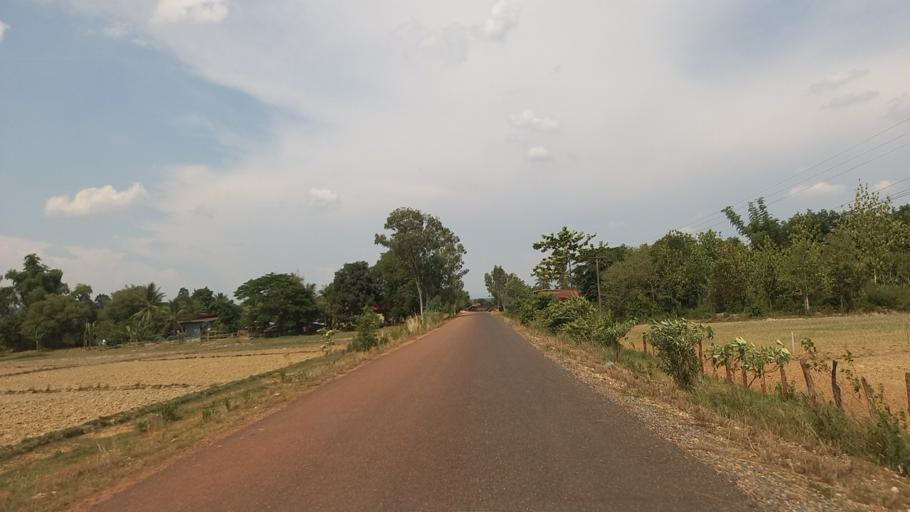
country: LA
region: Bolikhamxai
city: Muang Pakxan
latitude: 18.4298
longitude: 103.7367
